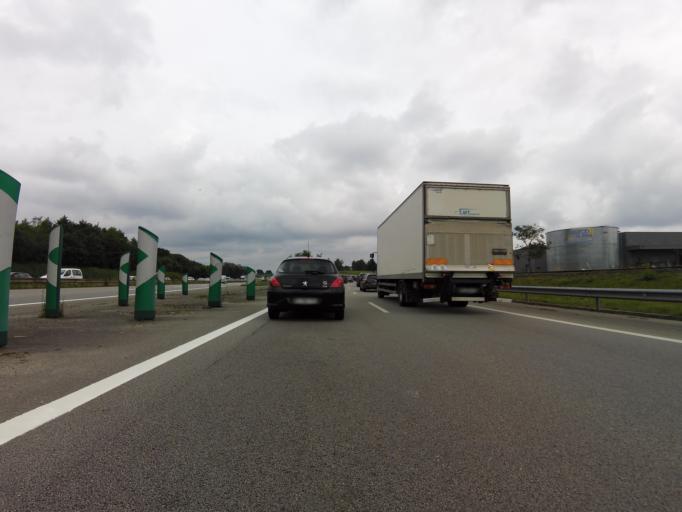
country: FR
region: Brittany
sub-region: Departement du Morbihan
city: Vannes
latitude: 47.6667
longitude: -2.7300
